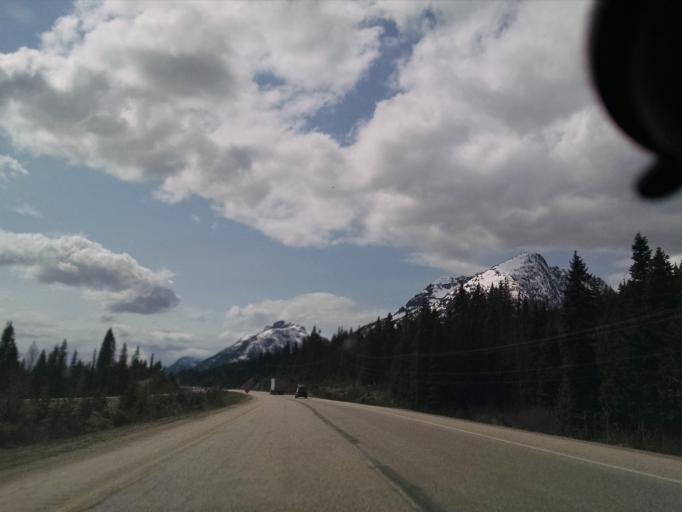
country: CA
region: British Columbia
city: Hope
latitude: 49.6225
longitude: -121.0379
